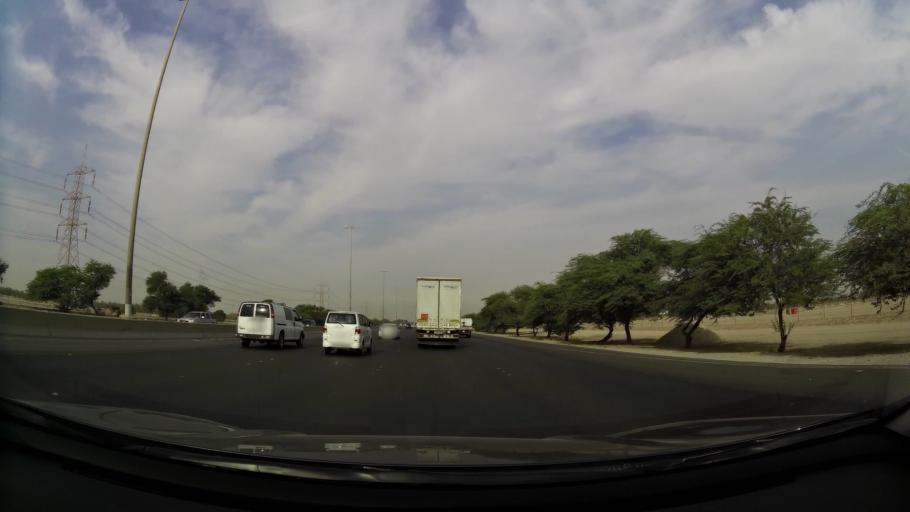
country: KW
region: Al Asimah
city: Ar Rabiyah
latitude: 29.2708
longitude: 47.8201
